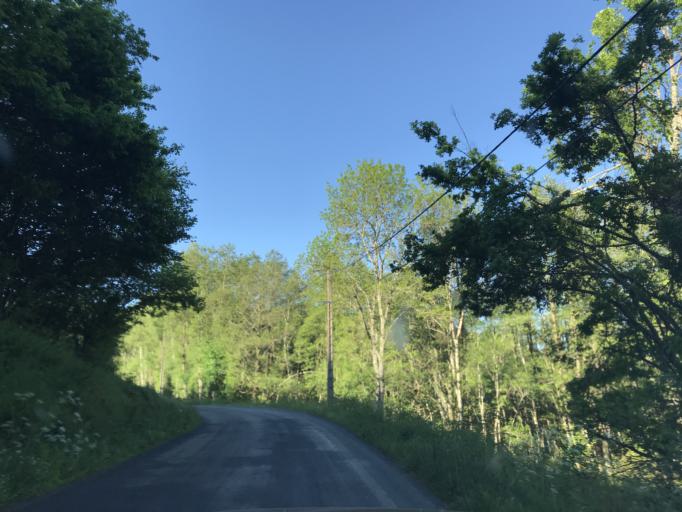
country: FR
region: Auvergne
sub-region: Departement du Puy-de-Dome
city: Job
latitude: 45.7004
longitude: 3.6935
